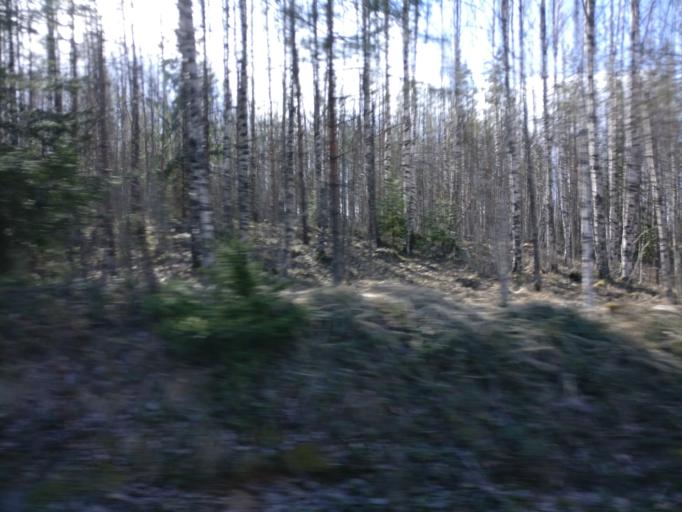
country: FI
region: Varsinais-Suomi
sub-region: Salo
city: Suomusjaervi
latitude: 60.3071
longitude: 23.6467
